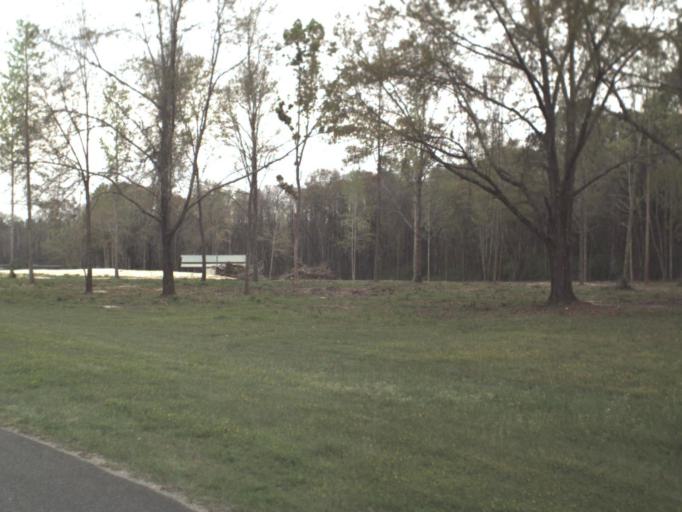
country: US
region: Florida
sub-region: Gulf County
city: Wewahitchka
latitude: 30.1337
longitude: -85.2078
